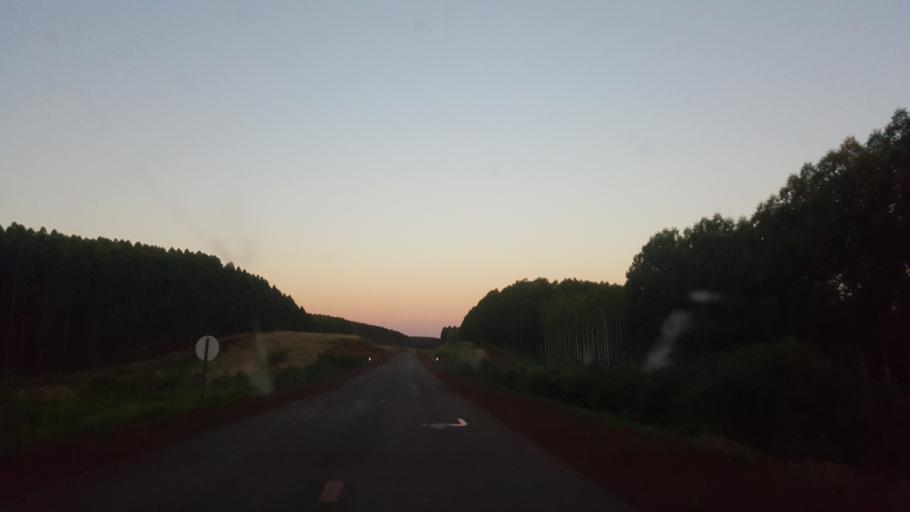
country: AR
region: Corrientes
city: Garruchos
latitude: -28.2523
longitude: -55.8491
